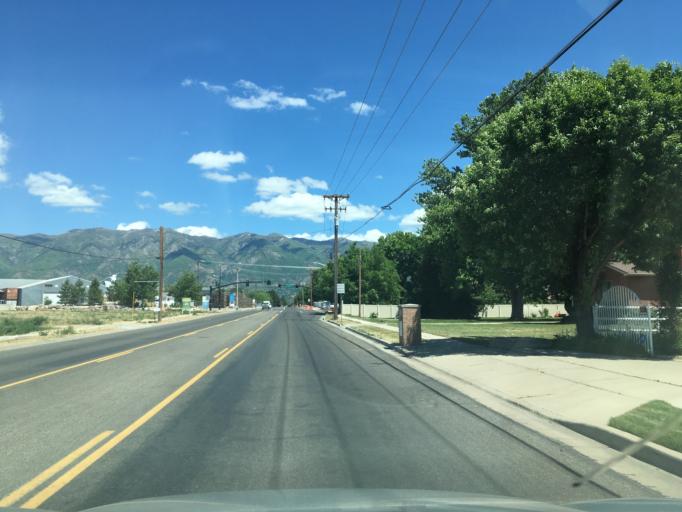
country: US
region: Utah
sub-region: Davis County
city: Layton
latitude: 41.0601
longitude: -111.9898
